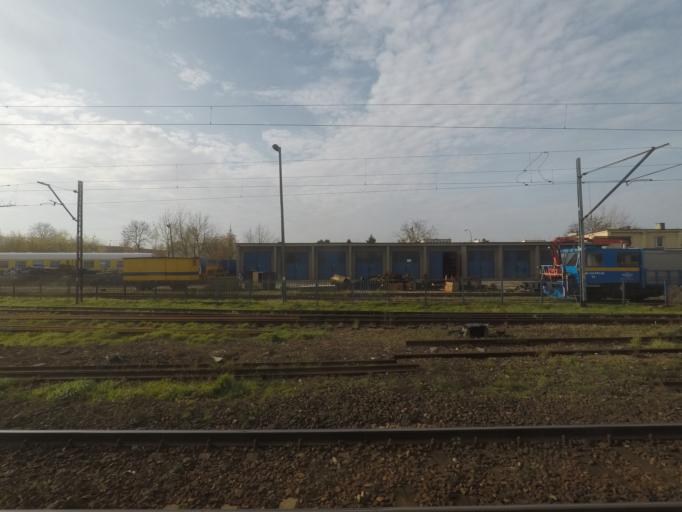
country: PL
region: Subcarpathian Voivodeship
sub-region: Rzeszow
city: Rzeszow
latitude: 50.0529
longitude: 21.9939
